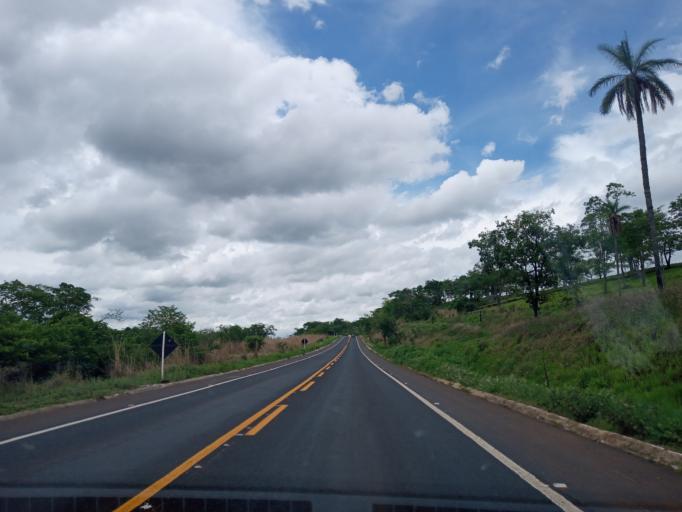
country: BR
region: Minas Gerais
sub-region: Uberaba
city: Uberaba
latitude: -19.2802
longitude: -47.6244
